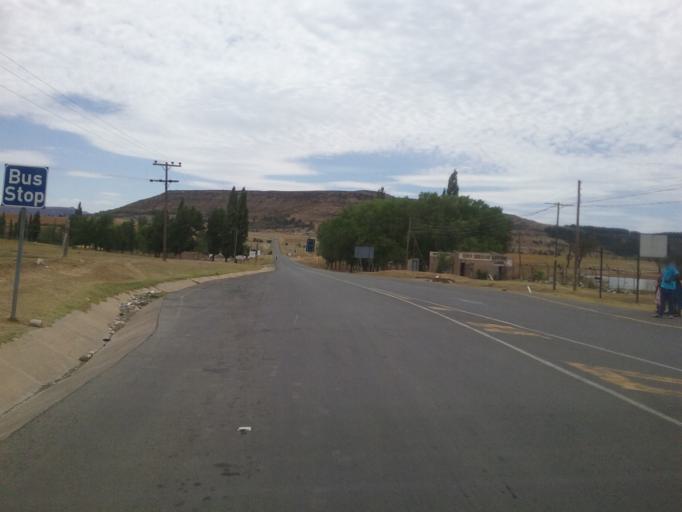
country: LS
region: Maseru
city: Nako
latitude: -29.6218
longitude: 27.4965
